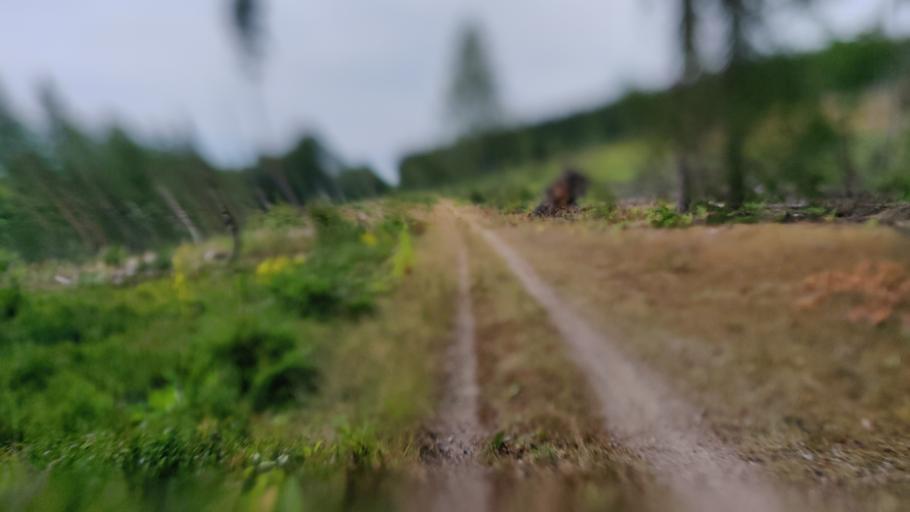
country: SE
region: Vaermland
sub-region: Hagfors Kommun
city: Hagfors
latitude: 60.0388
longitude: 13.5358
